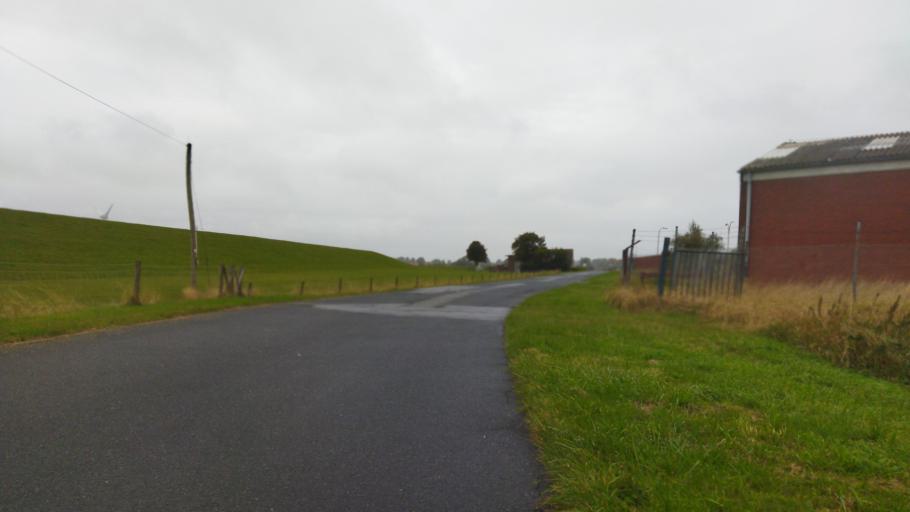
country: NL
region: Groningen
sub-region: Gemeente Delfzijl
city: Delfzijl
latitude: 53.3393
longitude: 7.0531
